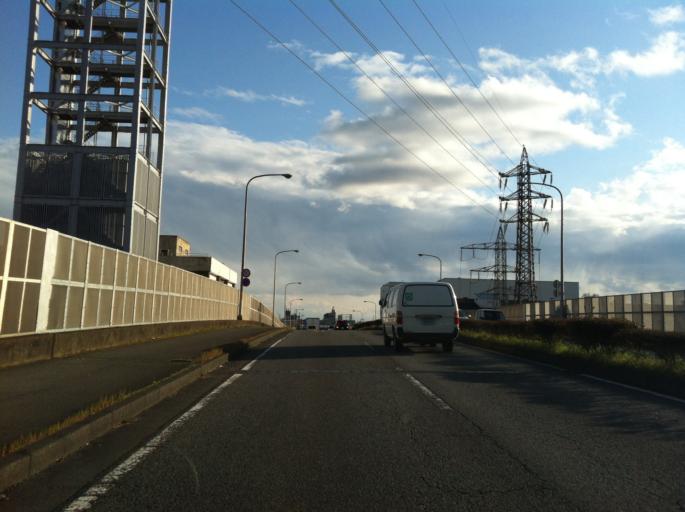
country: JP
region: Shizuoka
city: Fuji
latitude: 35.1509
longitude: 138.6640
